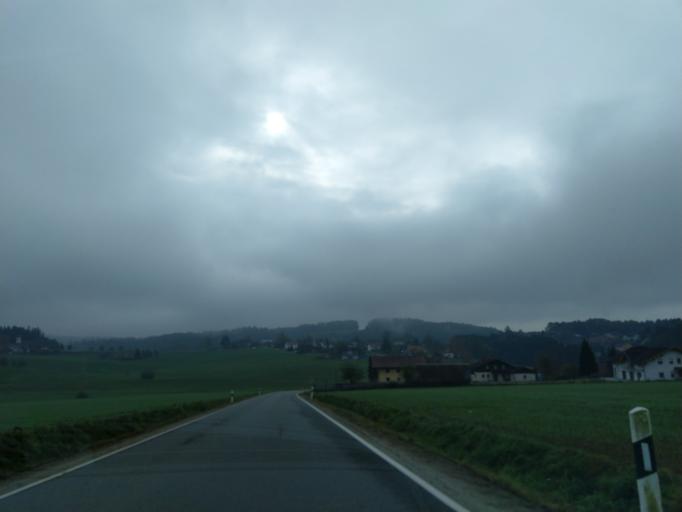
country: DE
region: Bavaria
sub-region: Lower Bavaria
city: Auerbach
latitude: 48.7881
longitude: 13.1128
